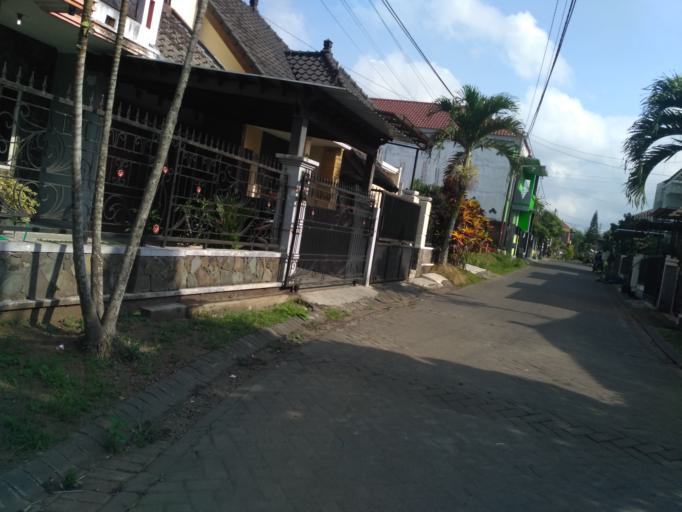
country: ID
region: East Java
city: Malang
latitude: -7.9363
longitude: 112.6139
